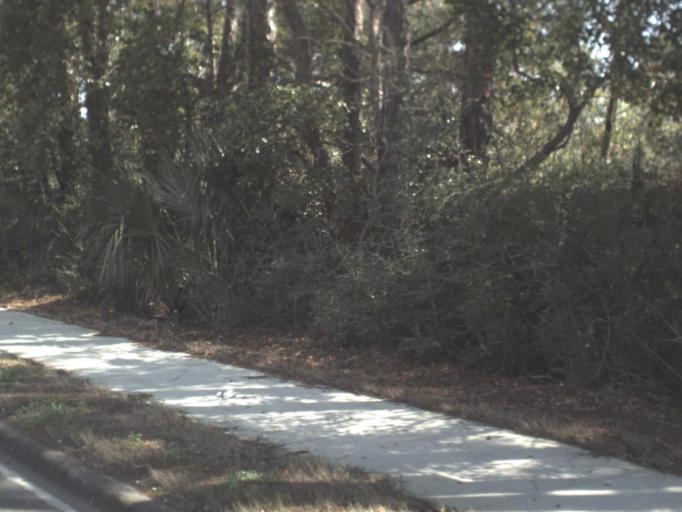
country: US
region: Florida
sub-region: Bay County
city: Hiland Park
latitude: 30.1895
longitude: -85.6530
